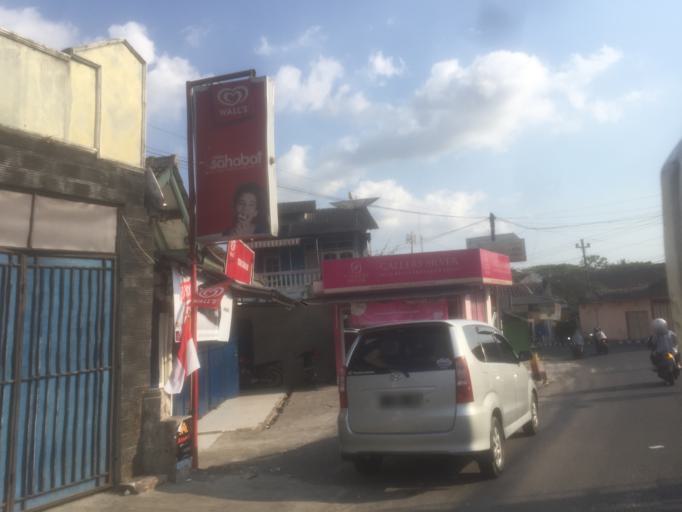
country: ID
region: Daerah Istimewa Yogyakarta
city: Sleman
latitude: -7.6652
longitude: 110.4195
